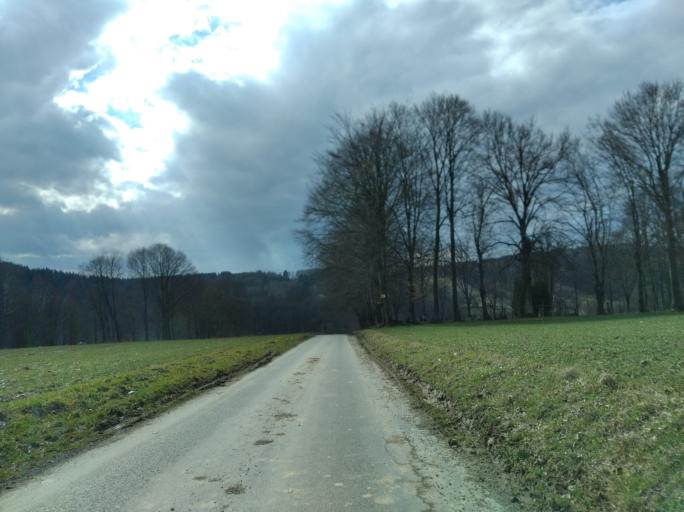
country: PL
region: Subcarpathian Voivodeship
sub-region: Powiat strzyzowski
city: Wysoka Strzyzowska
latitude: 49.7934
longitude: 21.7270
